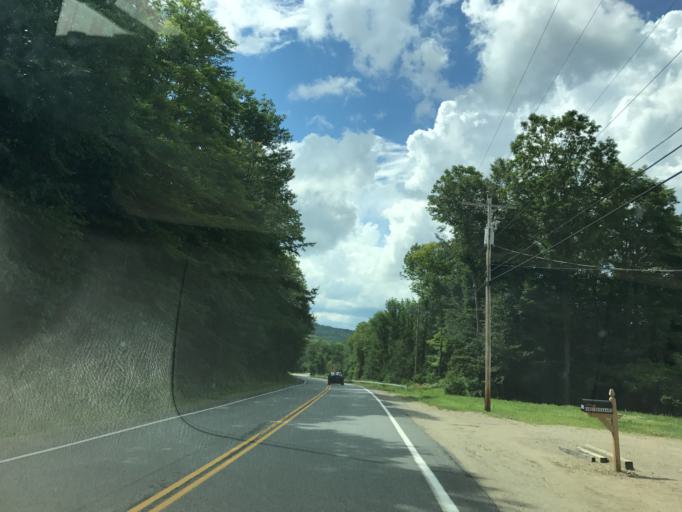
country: US
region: New York
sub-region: Saratoga County
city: Hadley
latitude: 43.4145
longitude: -73.9197
